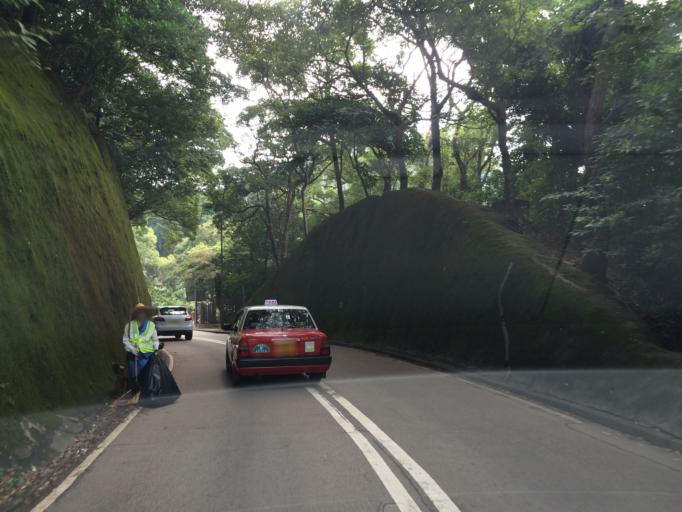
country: HK
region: Wanchai
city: Wan Chai
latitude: 22.2567
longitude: 114.2295
